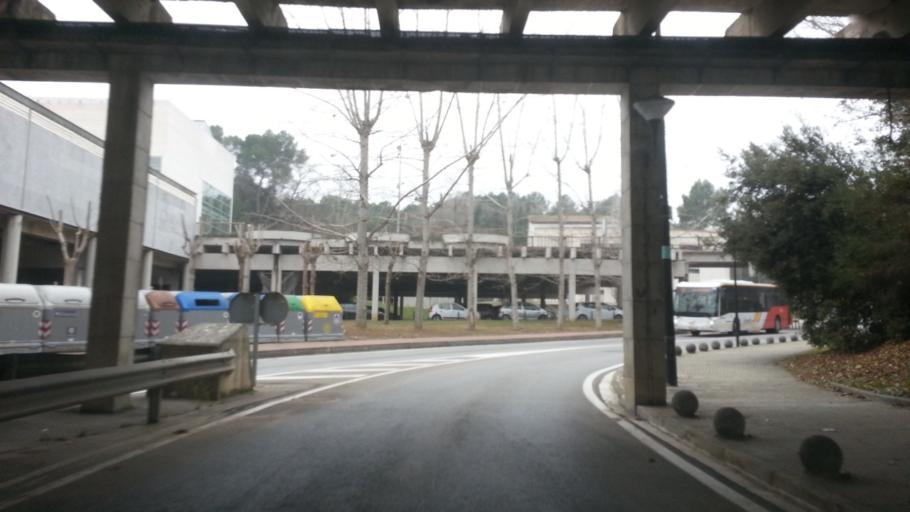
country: ES
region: Catalonia
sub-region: Provincia de Barcelona
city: Barbera del Valles
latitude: 41.5022
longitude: 2.1032
